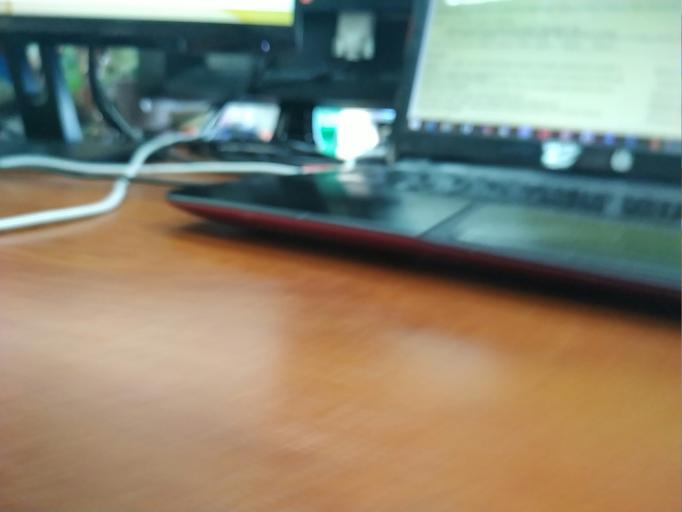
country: RU
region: Moskovskaya
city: Lozhki
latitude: 56.1922
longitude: 37.1898
